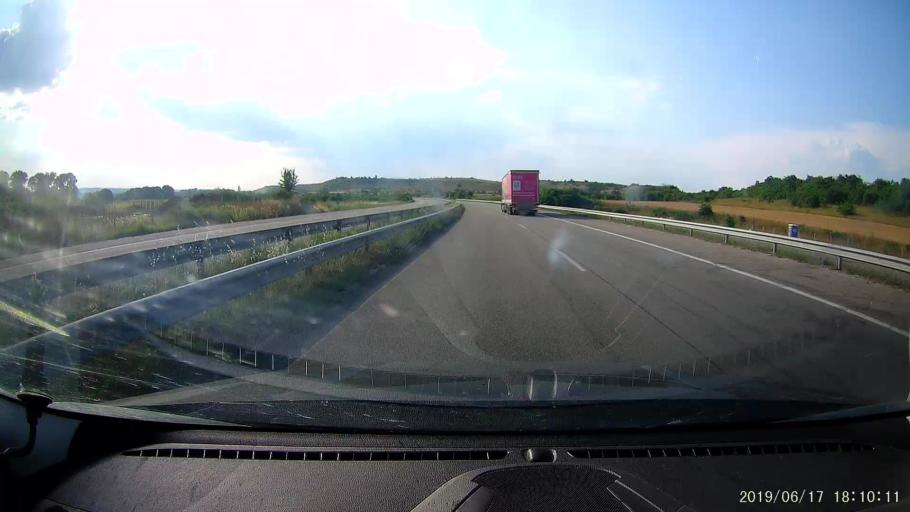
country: BG
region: Khaskovo
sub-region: Obshtina Lyubimets
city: Lyubimets
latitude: 41.8713
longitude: 26.0820
